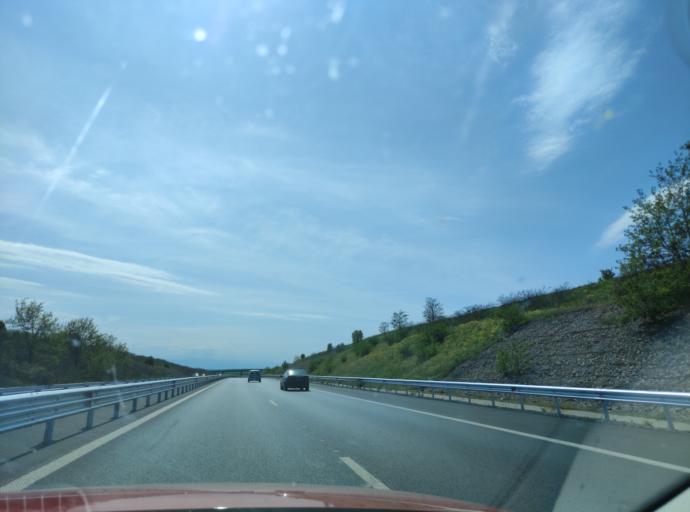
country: BG
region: Stara Zagora
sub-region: Obshtina Chirpan
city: Chirpan
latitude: 42.2021
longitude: 25.2869
